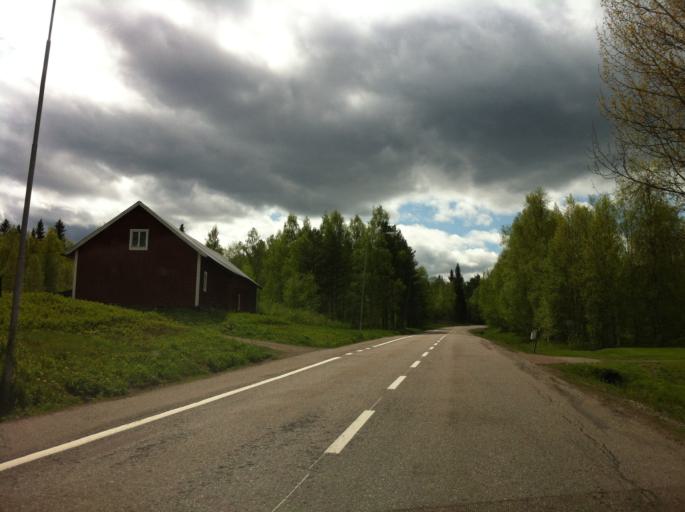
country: NO
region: Hedmark
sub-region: Trysil
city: Innbygda
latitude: 61.6905
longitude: 13.1396
